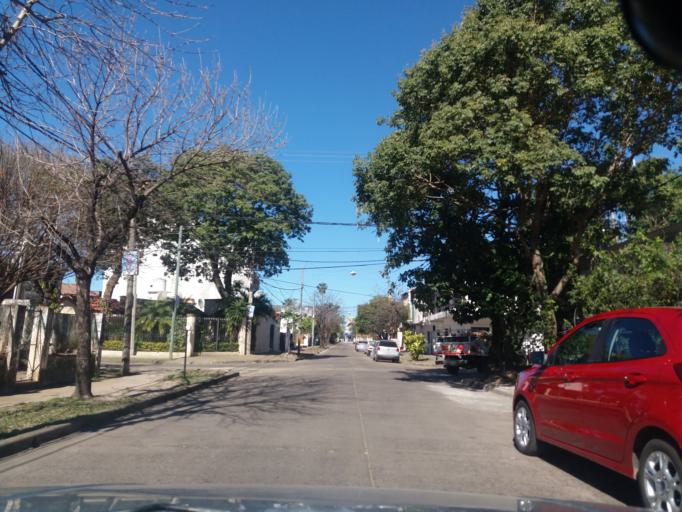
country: AR
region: Corrientes
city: Corrientes
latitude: -27.4758
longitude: -58.8200
